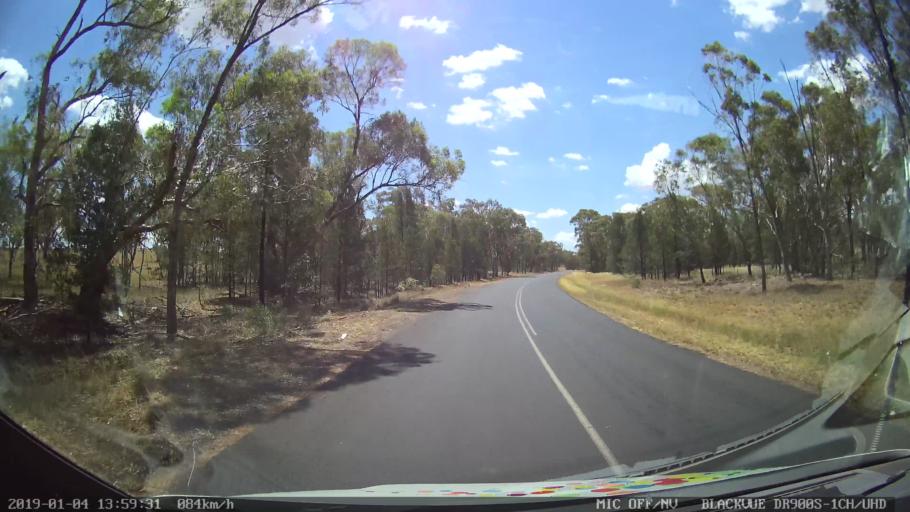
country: AU
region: New South Wales
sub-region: Dubbo Municipality
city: Dubbo
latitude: -32.3162
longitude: 148.5890
